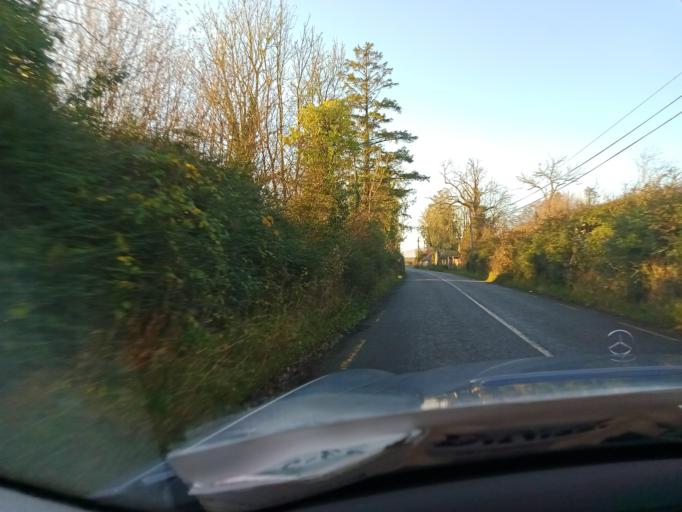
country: IE
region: Leinster
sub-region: Kilkenny
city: Callan
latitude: 52.5224
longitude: -7.3837
